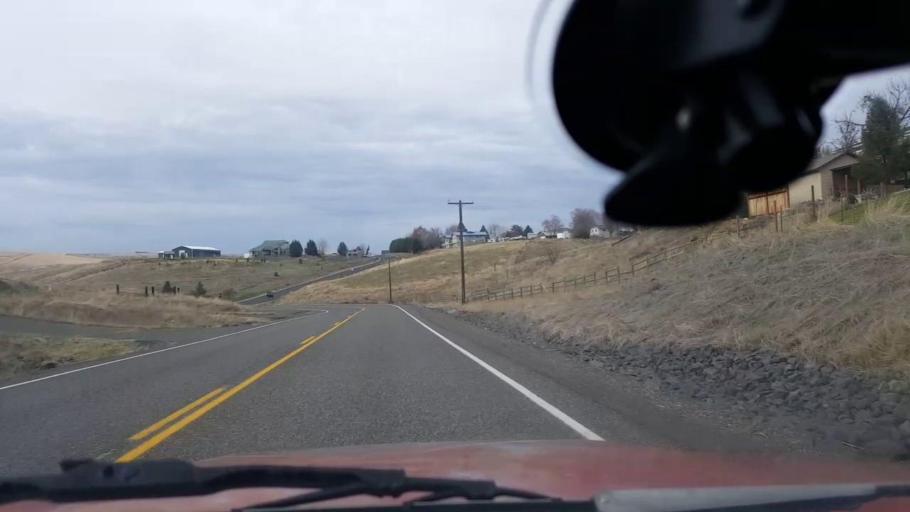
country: US
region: Washington
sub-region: Asotin County
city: Clarkston Heights-Vineland
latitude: 46.4020
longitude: -117.0861
